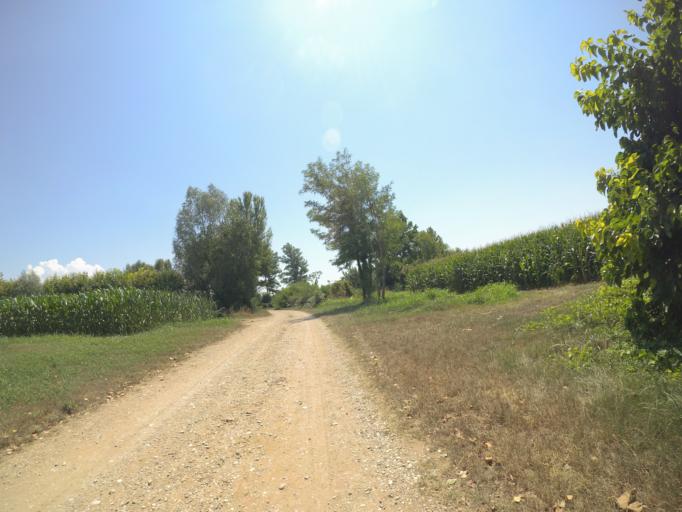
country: IT
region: Friuli Venezia Giulia
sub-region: Provincia di Udine
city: Mortegliano
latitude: 45.9401
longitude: 13.1788
